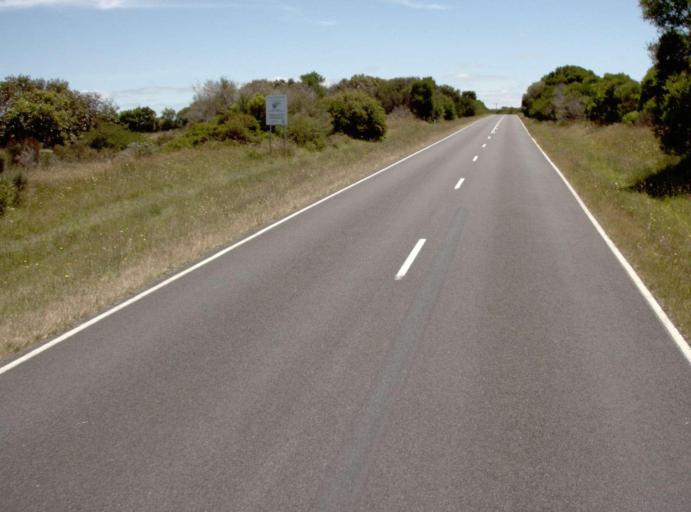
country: AU
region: Victoria
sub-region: Latrobe
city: Morwell
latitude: -38.8287
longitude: 146.2375
